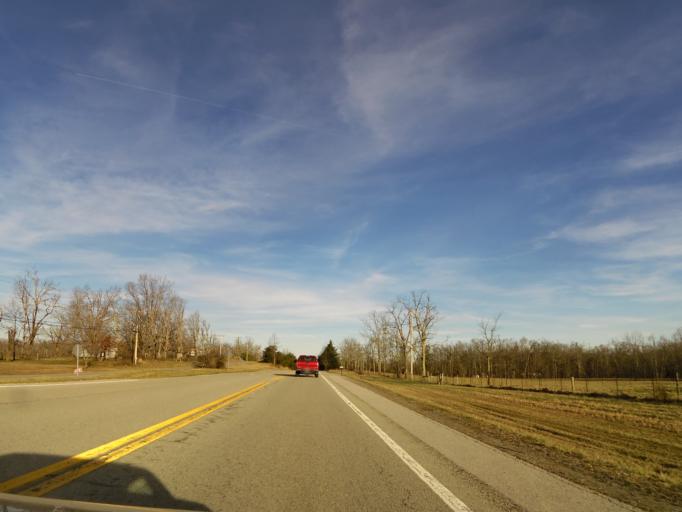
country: US
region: Tennessee
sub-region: Putnam County
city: Monterey
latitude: 35.9712
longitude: -85.2163
